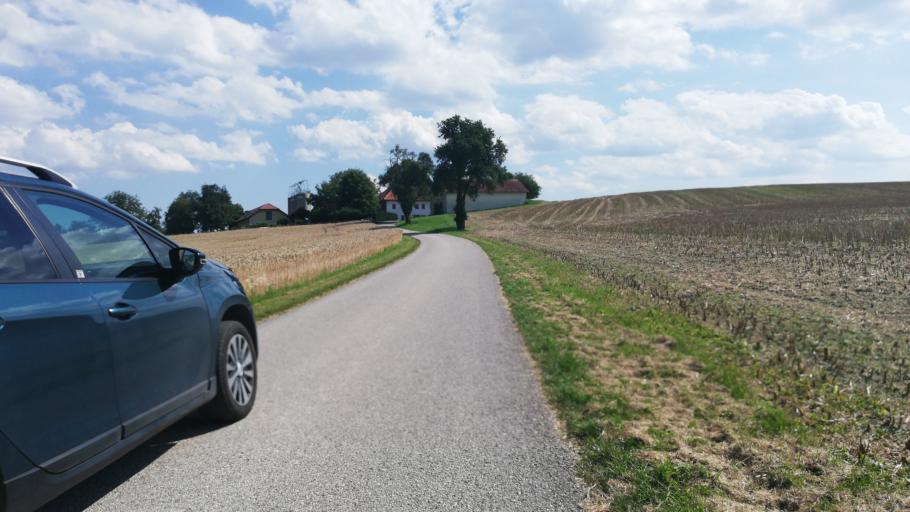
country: AT
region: Upper Austria
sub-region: Wels-Land
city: Pennewang
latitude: 48.1640
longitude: 13.8823
